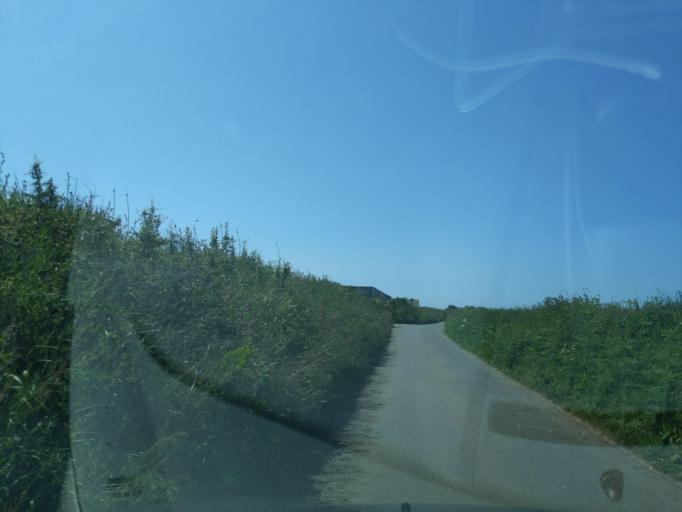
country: GB
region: England
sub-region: Cornwall
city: Wadebridge
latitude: 50.5816
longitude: -4.8376
